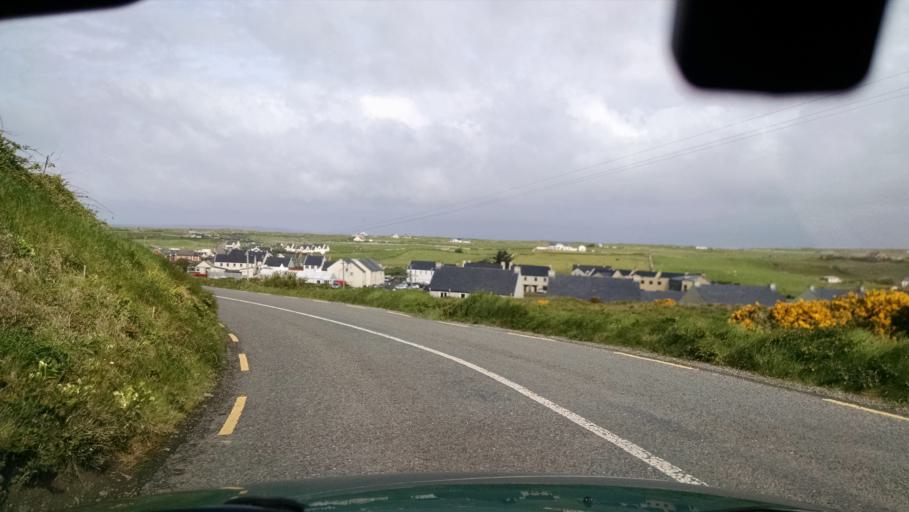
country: IE
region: Connaught
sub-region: County Galway
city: Bearna
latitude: 53.0149
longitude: -9.3732
